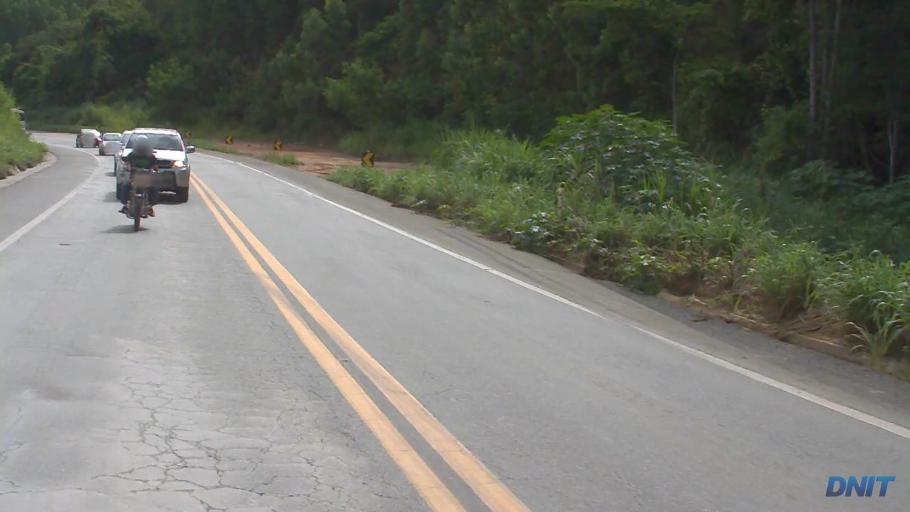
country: BR
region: Minas Gerais
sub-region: Ipaba
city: Ipaba
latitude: -19.3343
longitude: -42.4241
